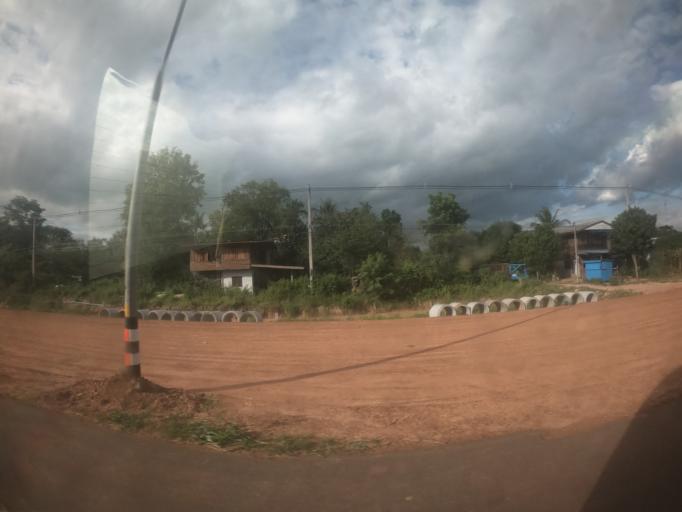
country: TH
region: Surin
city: Kap Choeng
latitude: 14.4998
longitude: 103.5643
